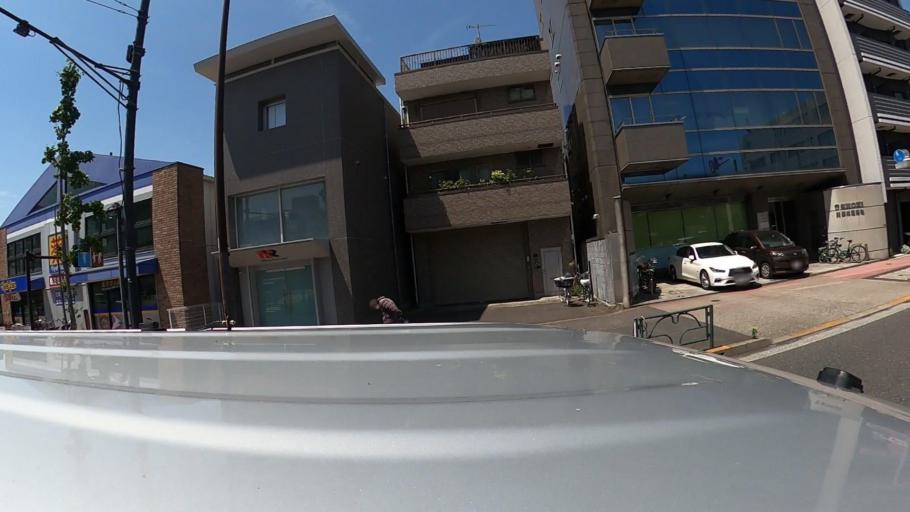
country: JP
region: Kanagawa
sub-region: Kawasaki-shi
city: Kawasaki
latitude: 35.5559
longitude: 139.7393
